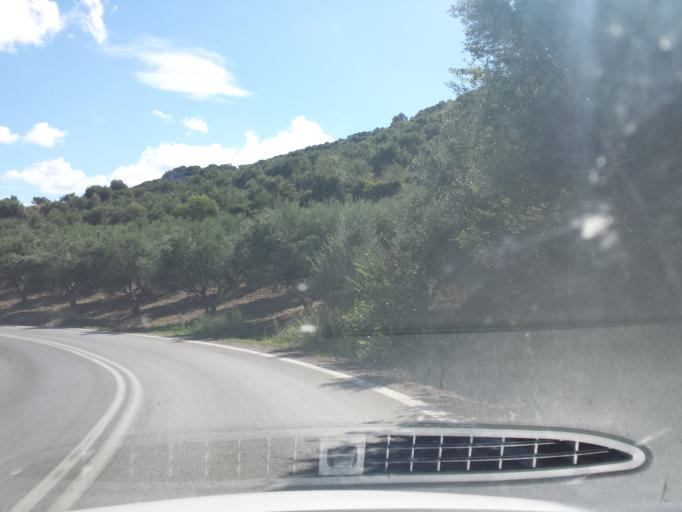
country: GR
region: Peloponnese
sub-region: Nomos Messinias
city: Pylos
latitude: 36.9315
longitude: 21.7316
